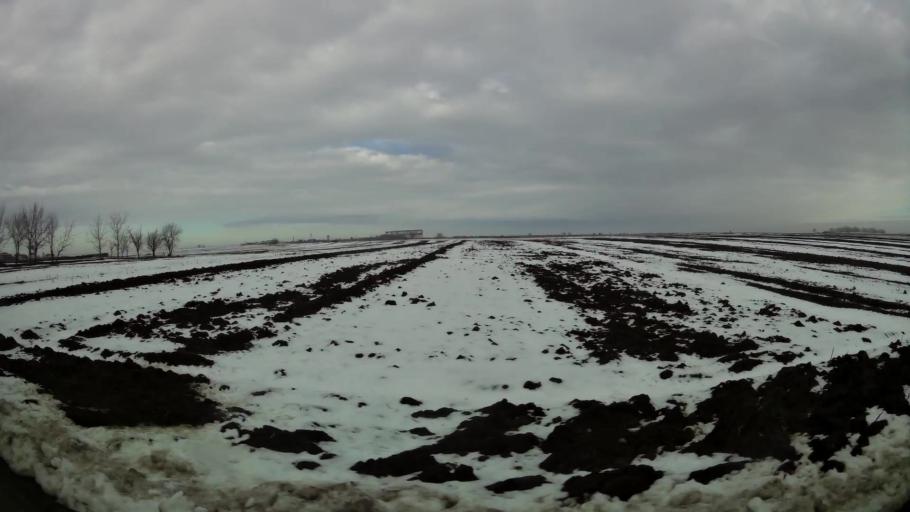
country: RS
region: Central Serbia
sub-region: Belgrade
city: Surcin
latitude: 44.8003
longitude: 20.3061
